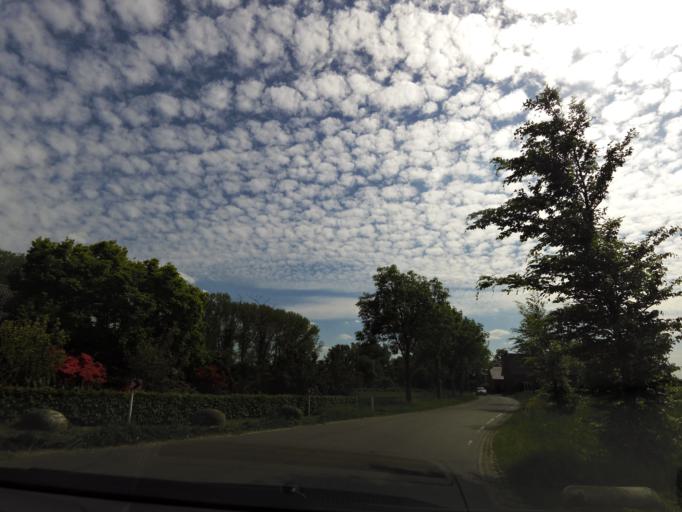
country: NL
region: Limburg
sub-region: Gemeente Roermond
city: Roermond
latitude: 51.1713
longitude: 5.9854
